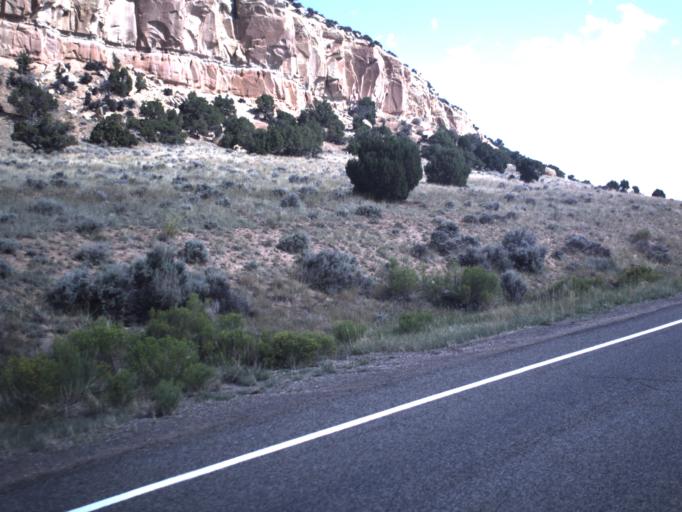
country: US
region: Utah
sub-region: Daggett County
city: Manila
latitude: 40.9323
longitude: -109.7039
